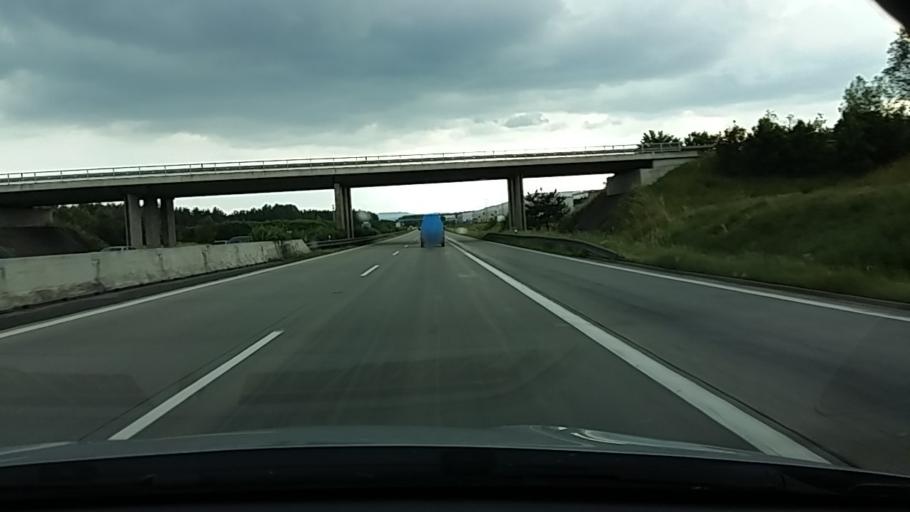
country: CZ
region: Plzensky
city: Bor
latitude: 49.7471
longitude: 12.7797
